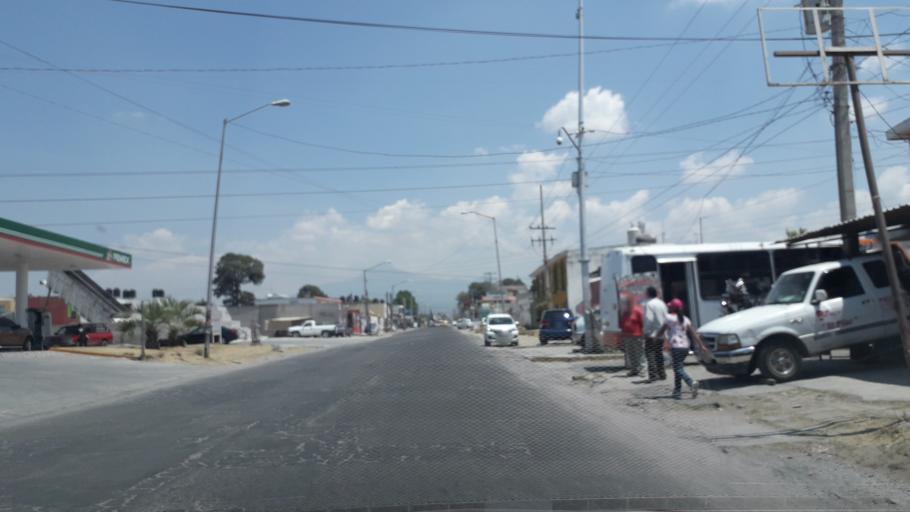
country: MX
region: Puebla
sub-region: Puebla
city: Primero de Mayo
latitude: 19.0735
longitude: -98.1143
